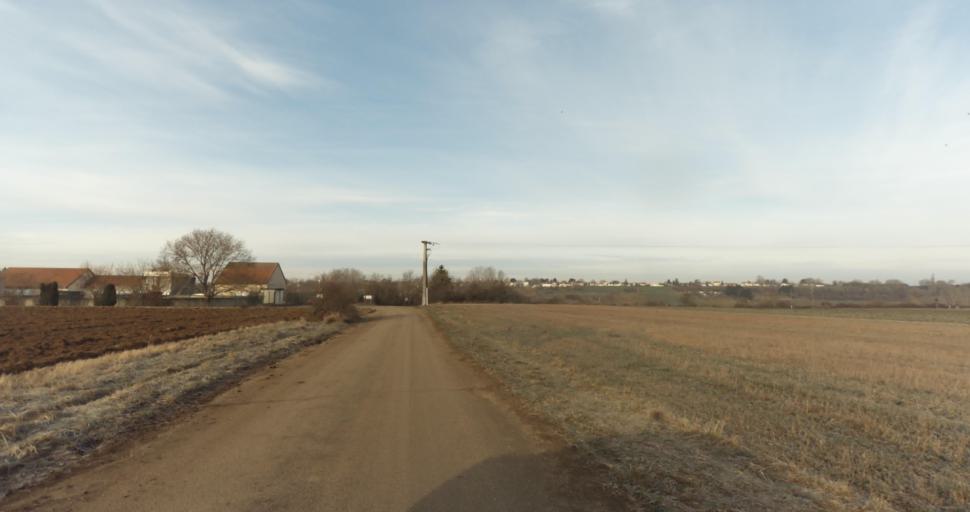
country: FR
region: Lorraine
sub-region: Departement de Meurthe-et-Moselle
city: Labry
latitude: 49.1736
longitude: 5.8953
